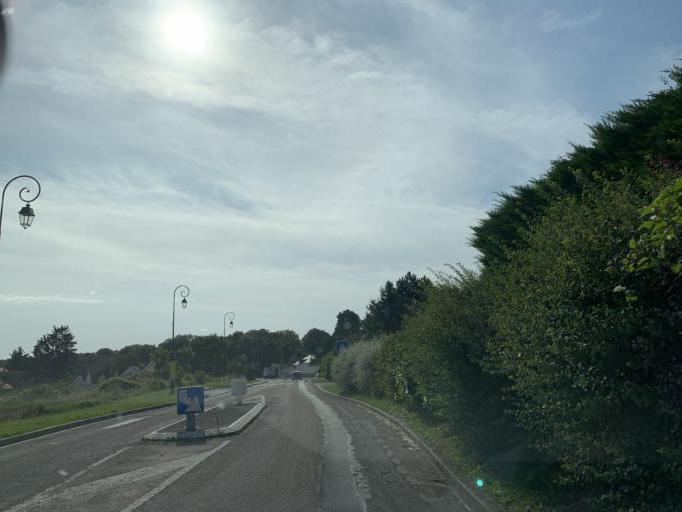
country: FR
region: Ile-de-France
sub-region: Departement de Seine-et-Marne
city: Annet-sur-Marne
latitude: 48.9311
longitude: 2.7169
